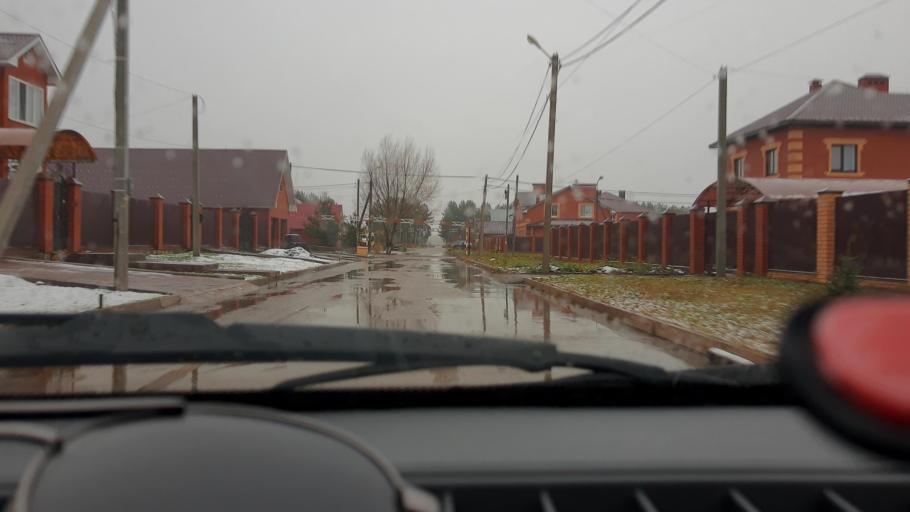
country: RU
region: Bashkortostan
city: Kabakovo
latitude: 54.6177
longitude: 56.1362
